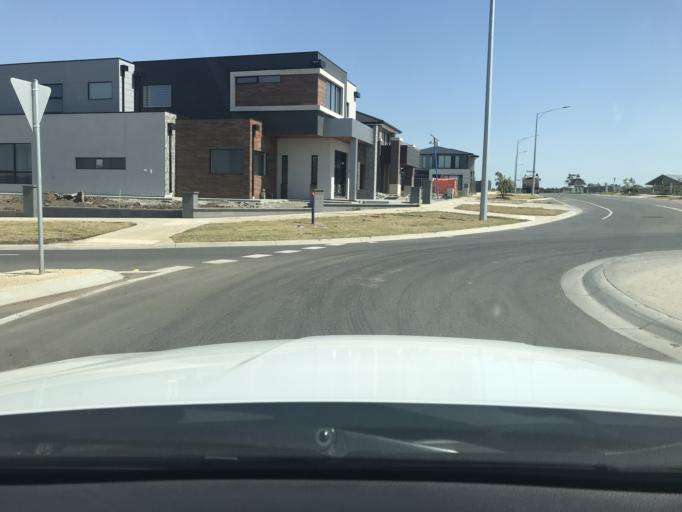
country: AU
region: Victoria
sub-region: Hume
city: Roxburgh Park
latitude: -37.5832
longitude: 144.8974
